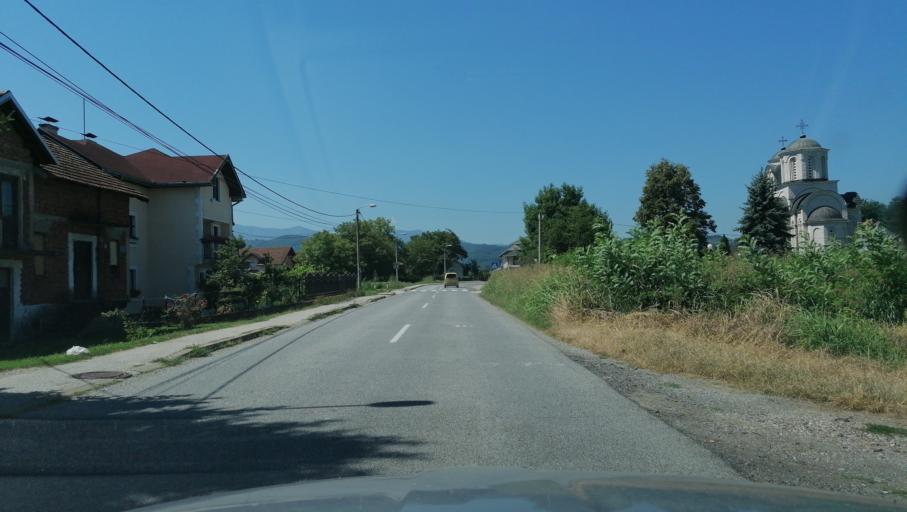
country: RS
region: Central Serbia
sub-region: Raski Okrug
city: Kraljevo
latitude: 43.6895
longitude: 20.6057
